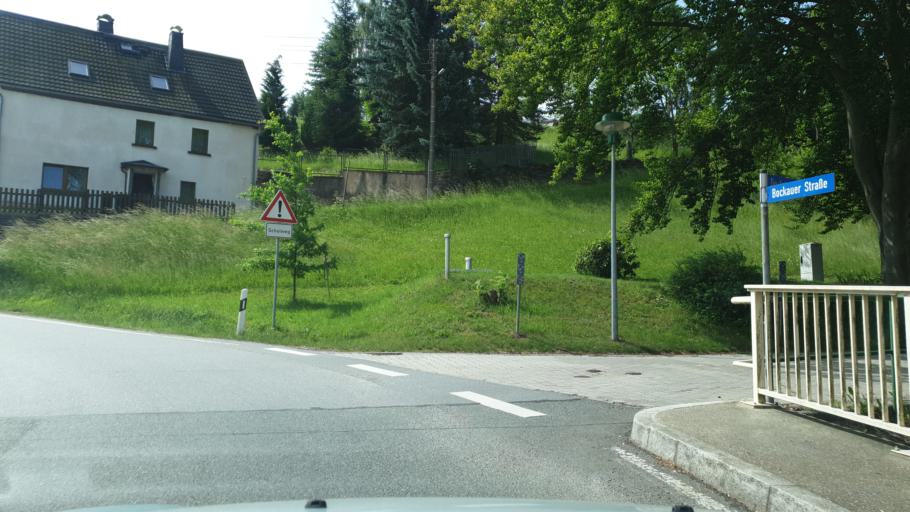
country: DE
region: Saxony
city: Zschorlau
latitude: 50.5516
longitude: 12.6601
